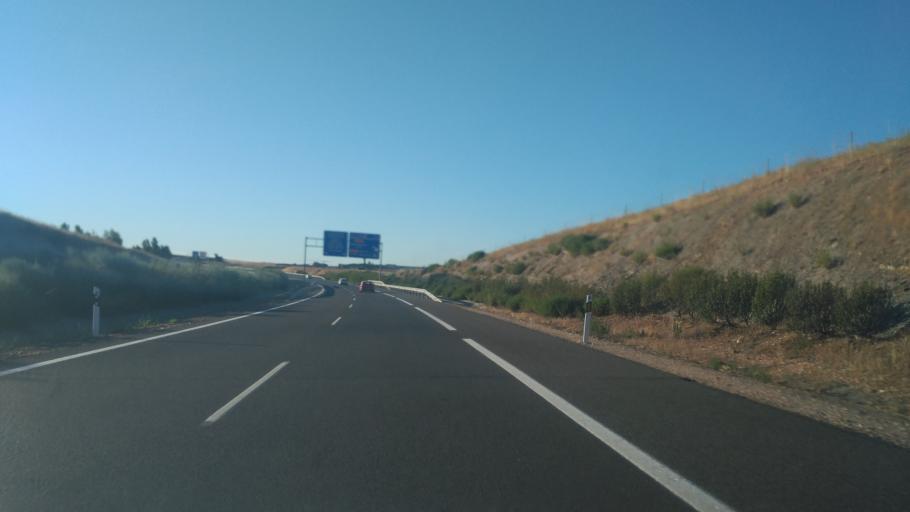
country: ES
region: Castille and Leon
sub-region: Provincia de Salamanca
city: Carbajosa de la Sagrada
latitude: 40.9141
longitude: -5.6610
